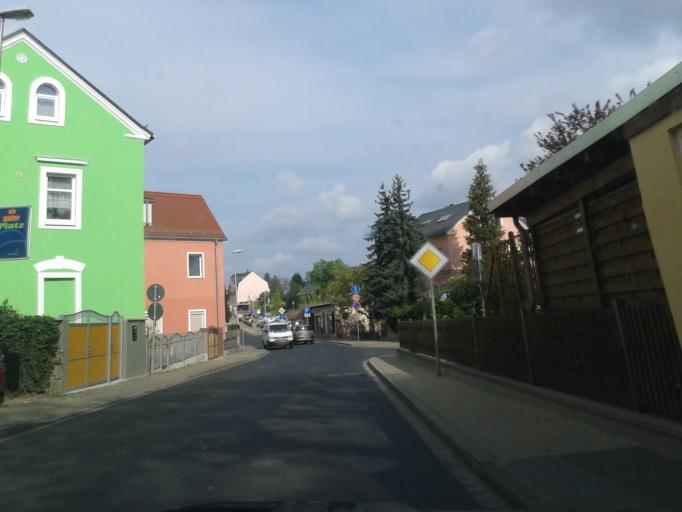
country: DE
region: Saxony
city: Radebeul
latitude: 51.1040
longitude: 13.6382
